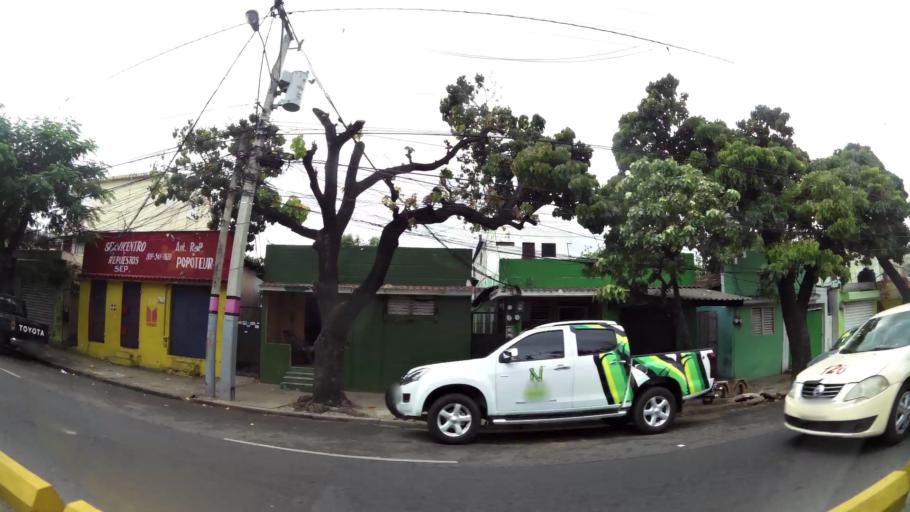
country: DO
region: Nacional
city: La Agustina
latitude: 18.4911
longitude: -69.9298
